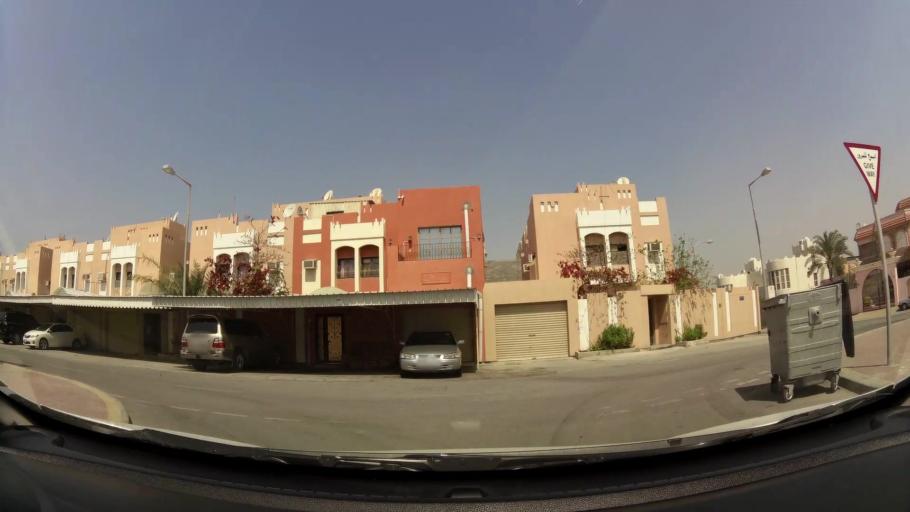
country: BH
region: Manama
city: Jidd Hafs
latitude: 26.2166
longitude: 50.4467
